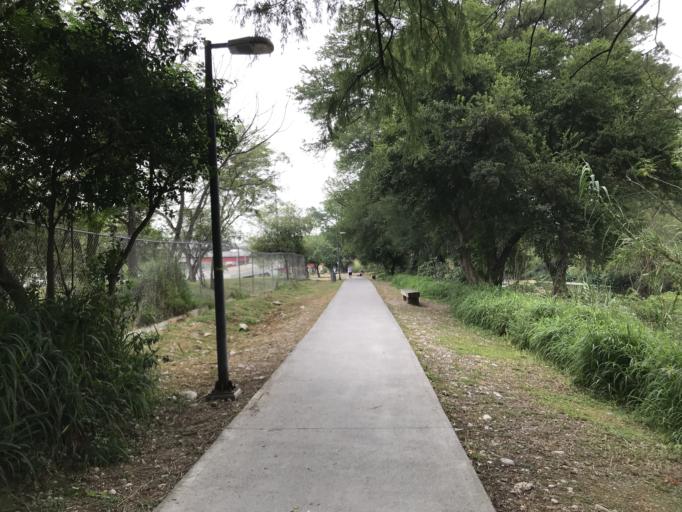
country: MX
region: Nuevo Leon
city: Guadalupe
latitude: 25.6718
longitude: -100.2465
